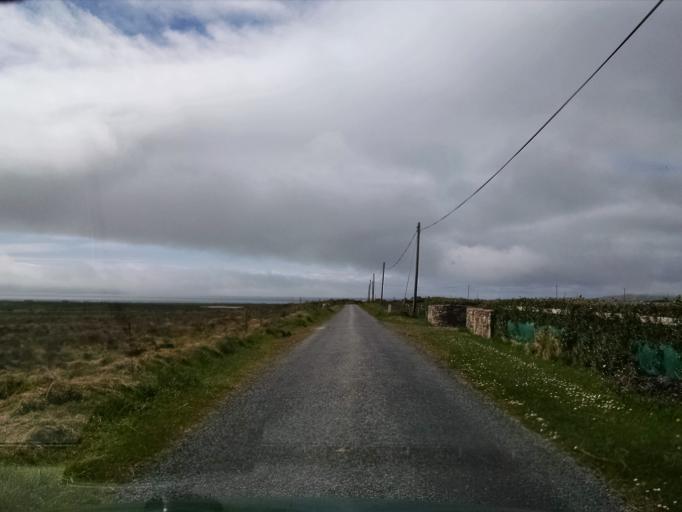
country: IE
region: Connaught
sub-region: County Galway
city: Clifden
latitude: 53.7395
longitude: -9.8583
